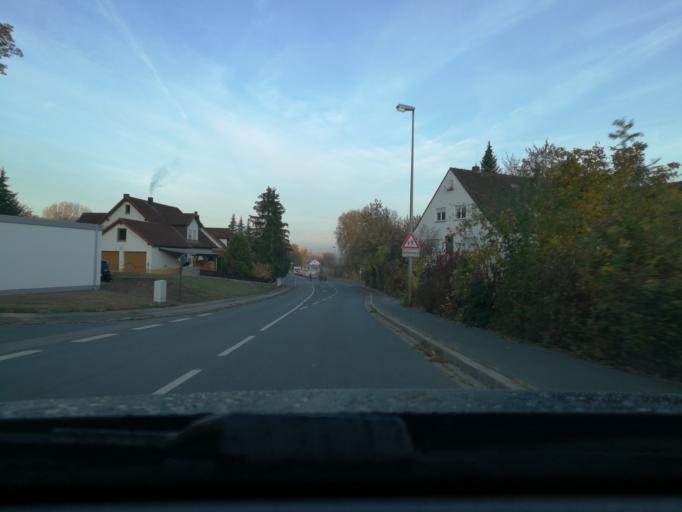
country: DE
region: Bavaria
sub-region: Regierungsbezirk Mittelfranken
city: Obermichelbach
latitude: 49.5576
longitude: 10.9189
